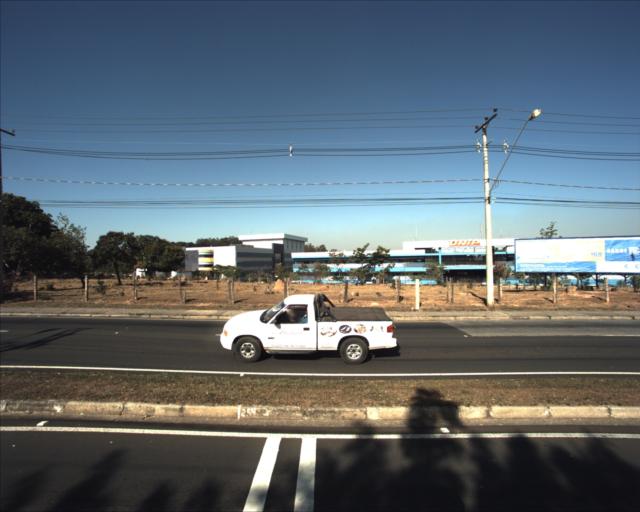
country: BR
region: Sao Paulo
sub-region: Sorocaba
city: Sorocaba
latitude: -23.4583
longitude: -47.4205
